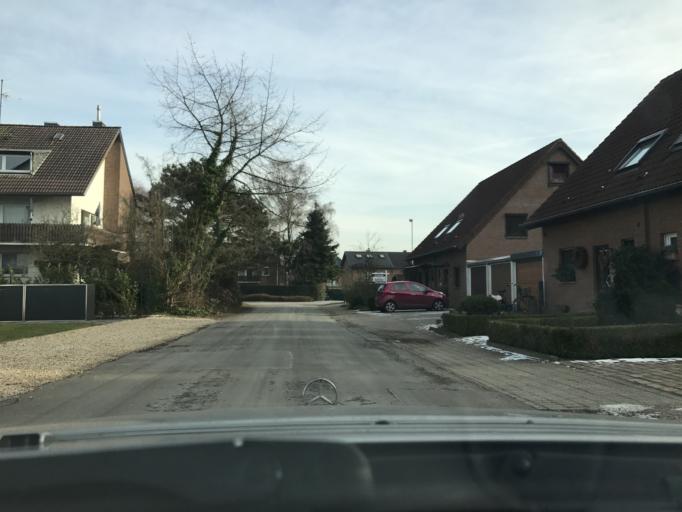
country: DE
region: North Rhine-Westphalia
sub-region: Regierungsbezirk Dusseldorf
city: Krefeld
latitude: 51.3490
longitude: 6.5966
